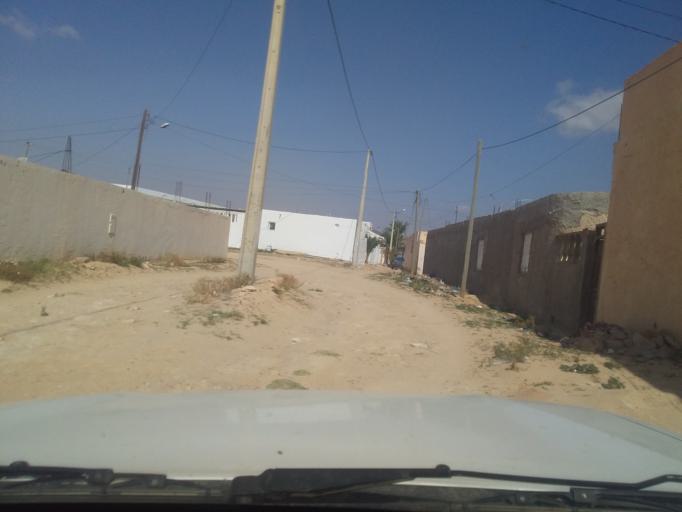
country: TN
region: Qabis
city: Gabes
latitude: 33.6248
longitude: 10.2799
